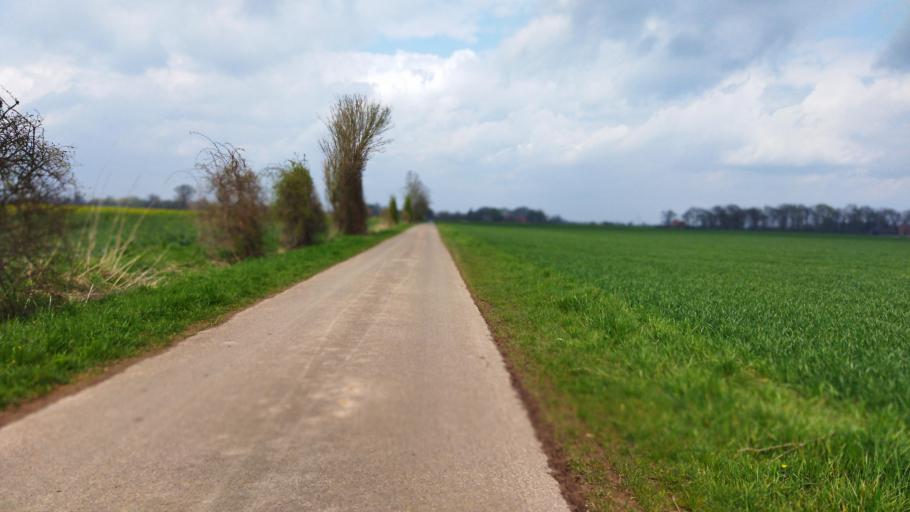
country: DE
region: Lower Saxony
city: Hilgermissen
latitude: 52.8786
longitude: 9.1717
